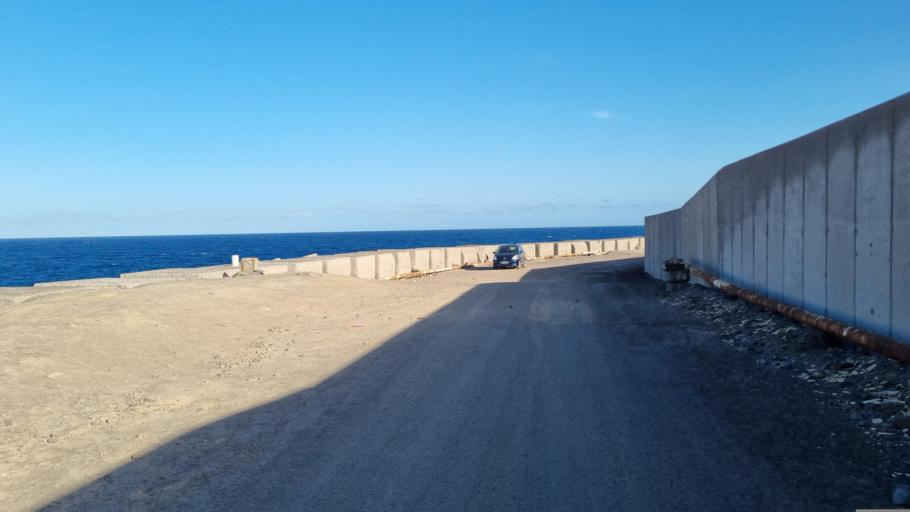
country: ES
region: Canary Islands
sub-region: Provincia de Santa Cruz de Tenerife
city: San Isidro
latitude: 28.0874
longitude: -16.4912
